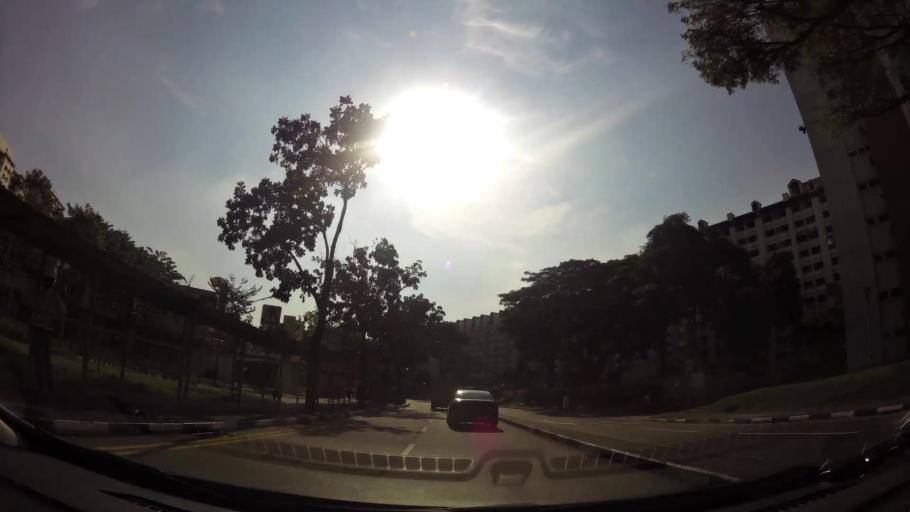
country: SG
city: Singapore
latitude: 1.3401
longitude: 103.8534
